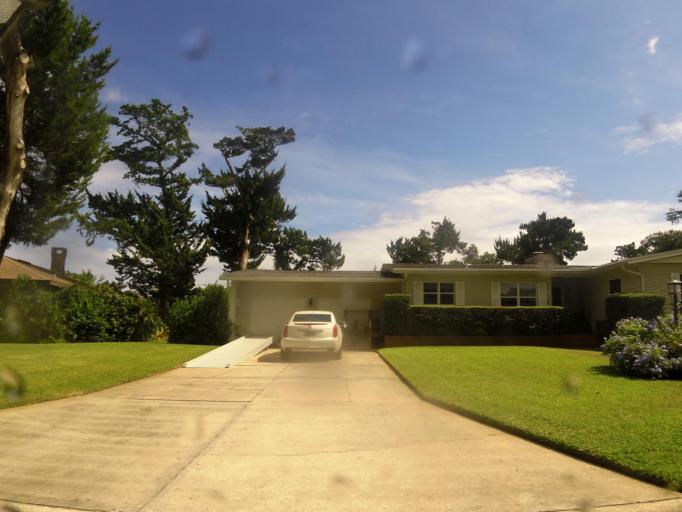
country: US
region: Florida
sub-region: Saint Johns County
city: Saint Augustine
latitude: 29.8980
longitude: -81.3023
